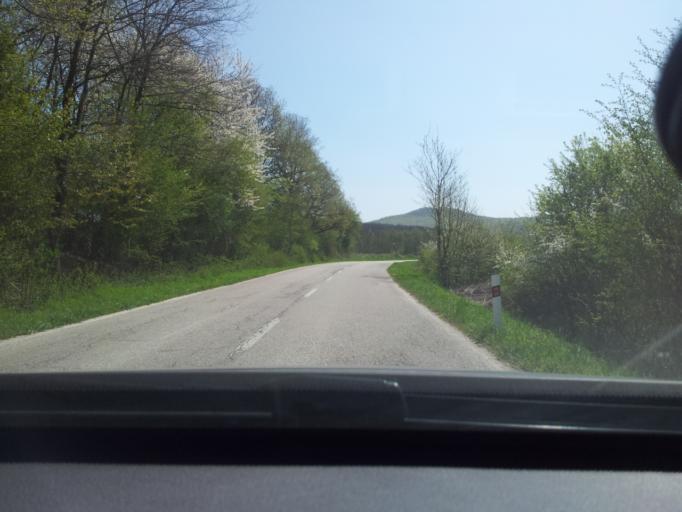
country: SK
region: Nitriansky
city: Partizanske
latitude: 48.5343
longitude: 18.3585
